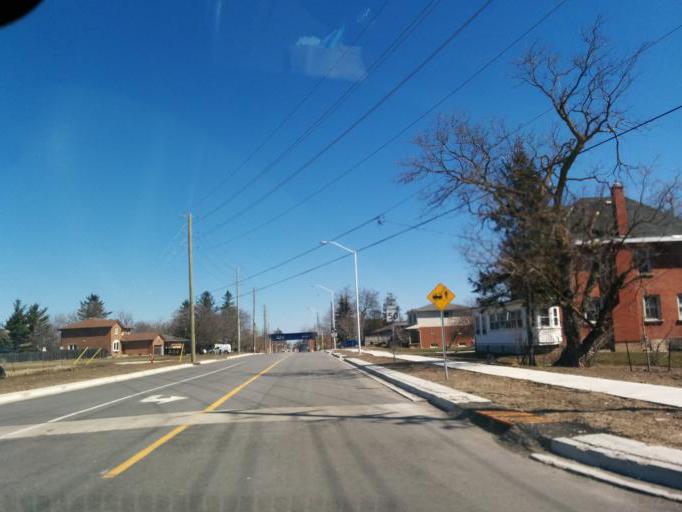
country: CA
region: Ontario
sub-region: Halton
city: Milton
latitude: 43.5062
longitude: -79.8907
